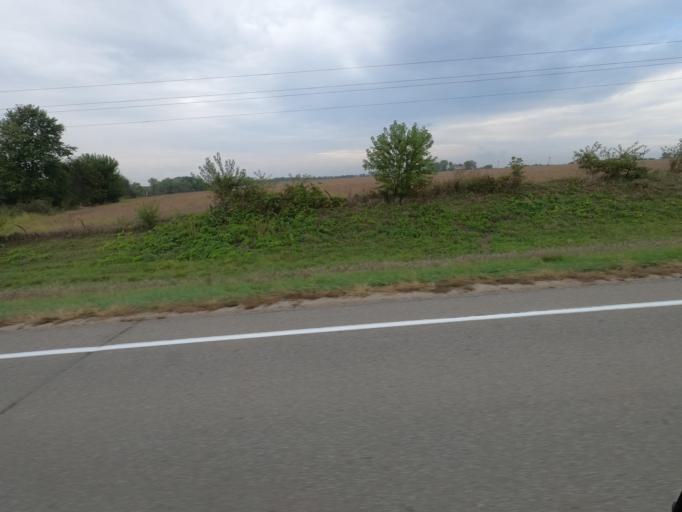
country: US
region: Iowa
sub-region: Henry County
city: Mount Pleasant
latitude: 40.8135
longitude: -91.7210
